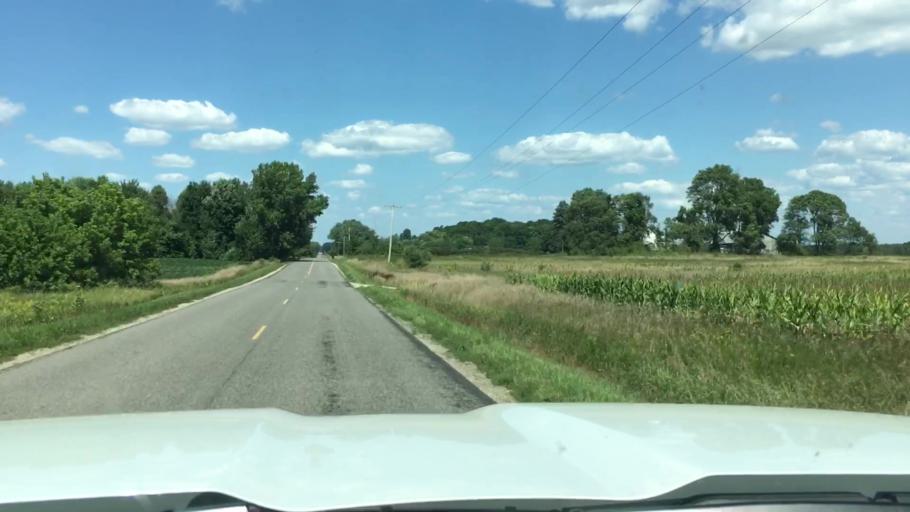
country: US
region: Michigan
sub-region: Muskegon County
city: Ravenna
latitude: 43.2386
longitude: -85.9179
